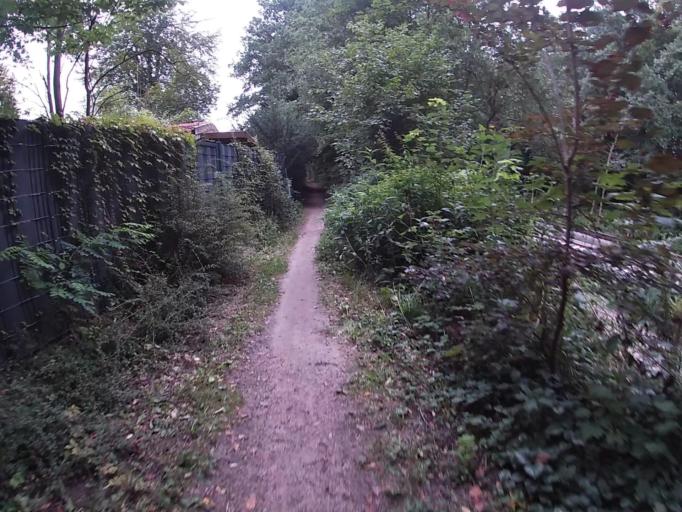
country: DE
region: Lower Saxony
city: Adendorf
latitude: 53.2837
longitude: 10.4555
